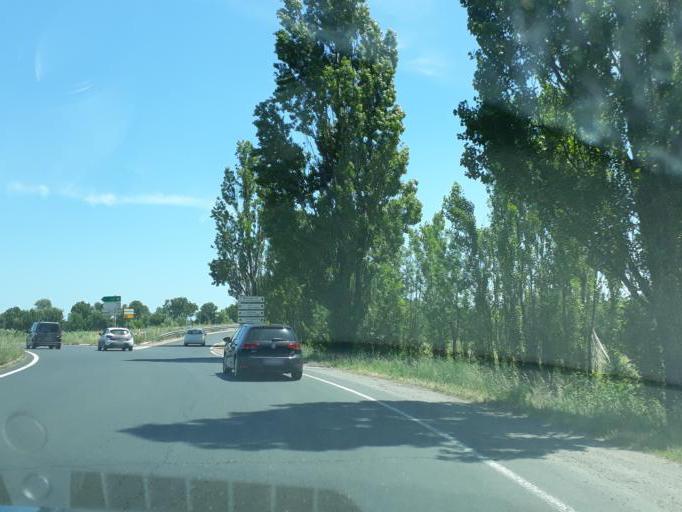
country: FR
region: Languedoc-Roussillon
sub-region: Departement de l'Herault
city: Villeneuve-les-Beziers
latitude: 43.3206
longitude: 3.2917
